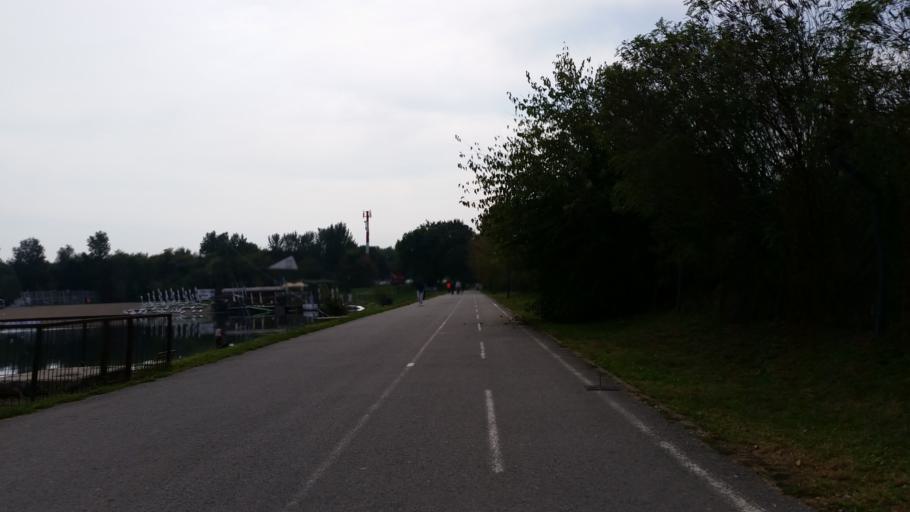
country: RS
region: Central Serbia
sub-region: Belgrade
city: Cukarica
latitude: 44.7776
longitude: 20.3728
